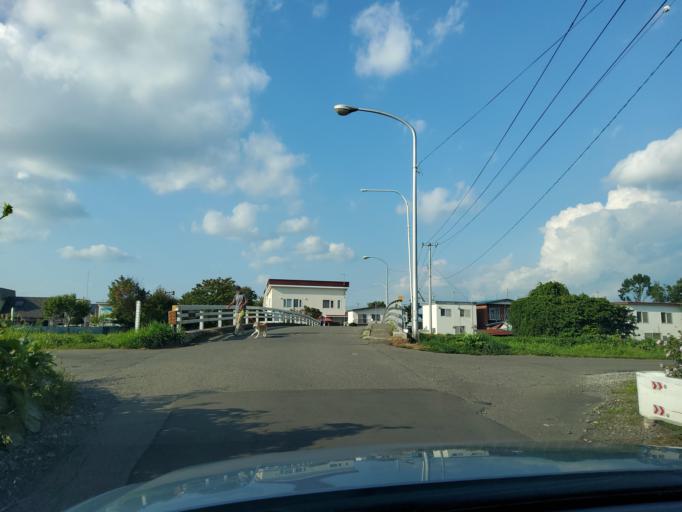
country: JP
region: Hokkaido
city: Obihiro
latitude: 42.8946
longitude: 143.1976
